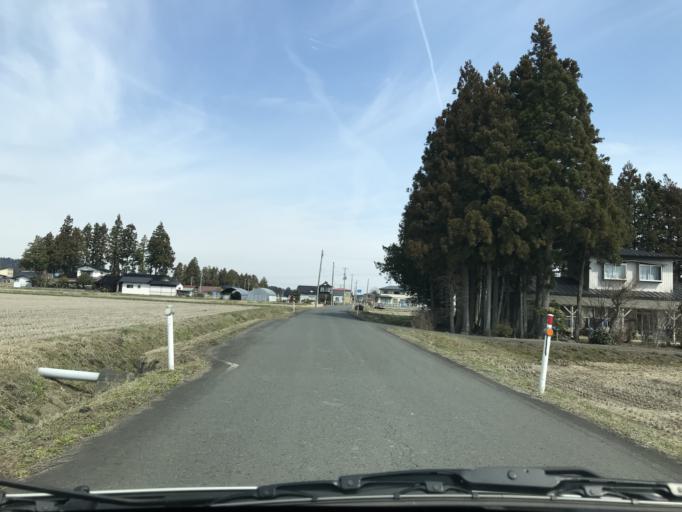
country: JP
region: Iwate
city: Mizusawa
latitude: 39.1270
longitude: 141.0482
